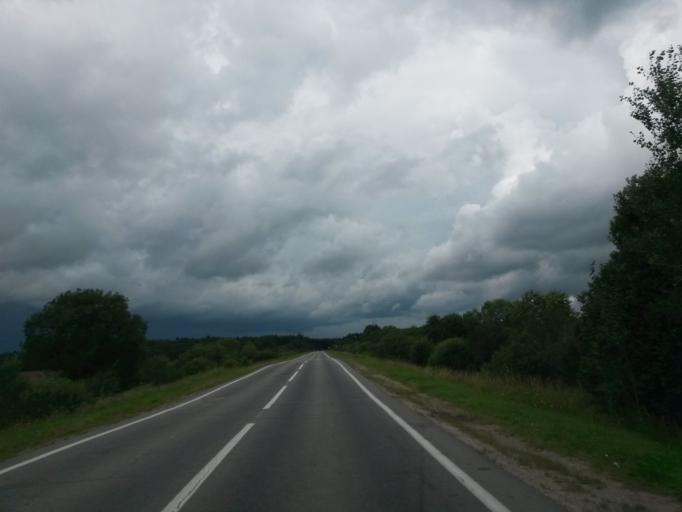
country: RU
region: Jaroslavl
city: Konstantinovskiy
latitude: 57.8490
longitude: 39.6318
